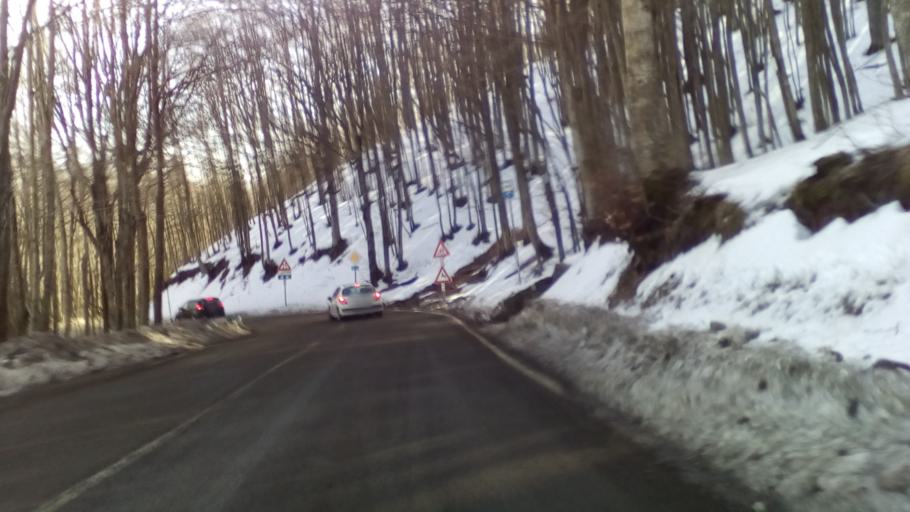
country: IT
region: Tuscany
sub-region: Provincia di Lucca
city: Fosciandora
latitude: 44.1975
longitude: 10.5063
